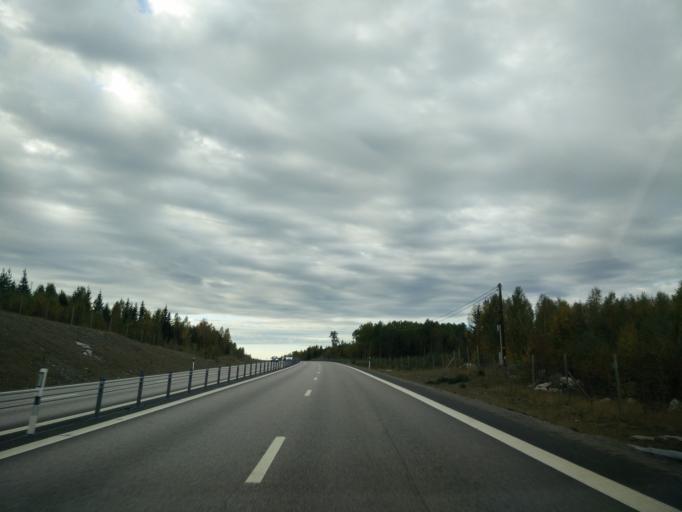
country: SE
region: Gaevleborg
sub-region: Hudiksvalls Kommun
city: Iggesund
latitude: 61.6818
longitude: 17.0392
